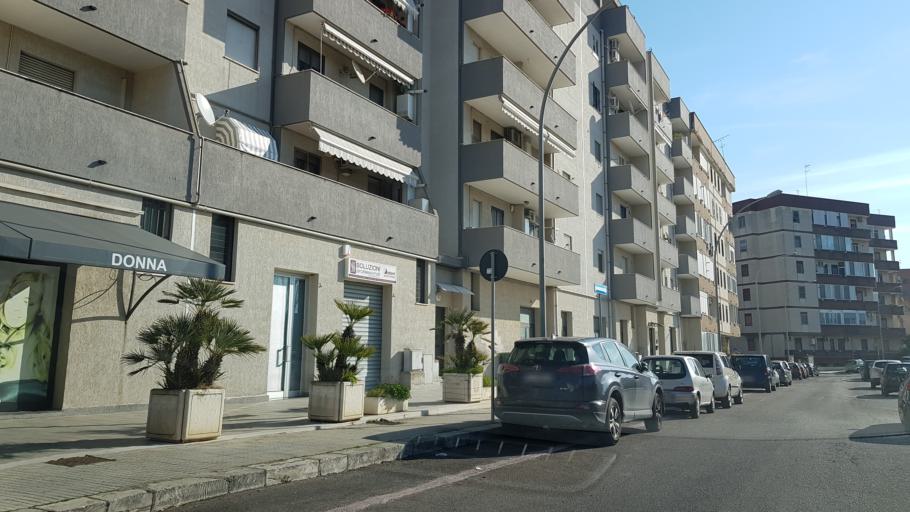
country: IT
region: Apulia
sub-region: Provincia di Brindisi
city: Brindisi
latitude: 40.6230
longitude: 17.9297
